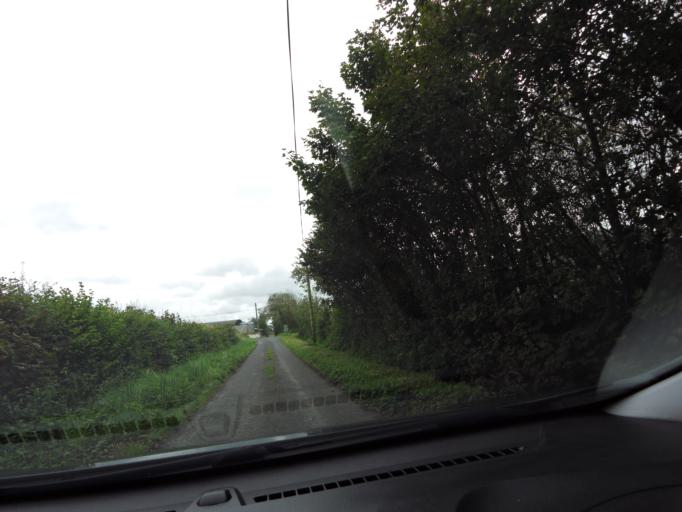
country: IE
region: Connaught
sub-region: County Galway
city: Athenry
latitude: 53.2962
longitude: -8.6830
